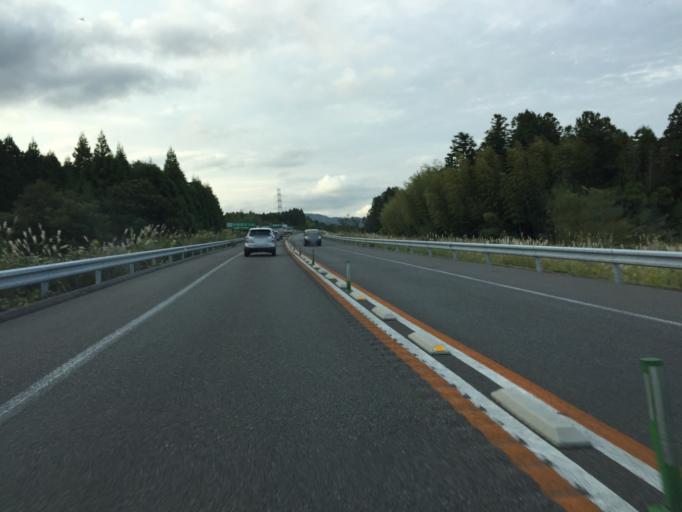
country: JP
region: Fukushima
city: Namie
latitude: 37.3563
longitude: 140.9745
